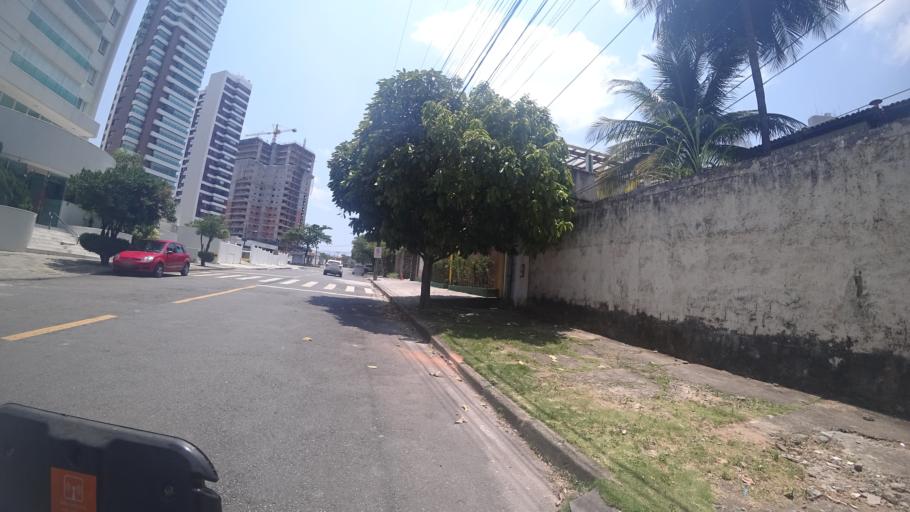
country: BR
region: Bahia
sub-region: Salvador
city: Salvador
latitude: -12.9887
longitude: -38.4540
